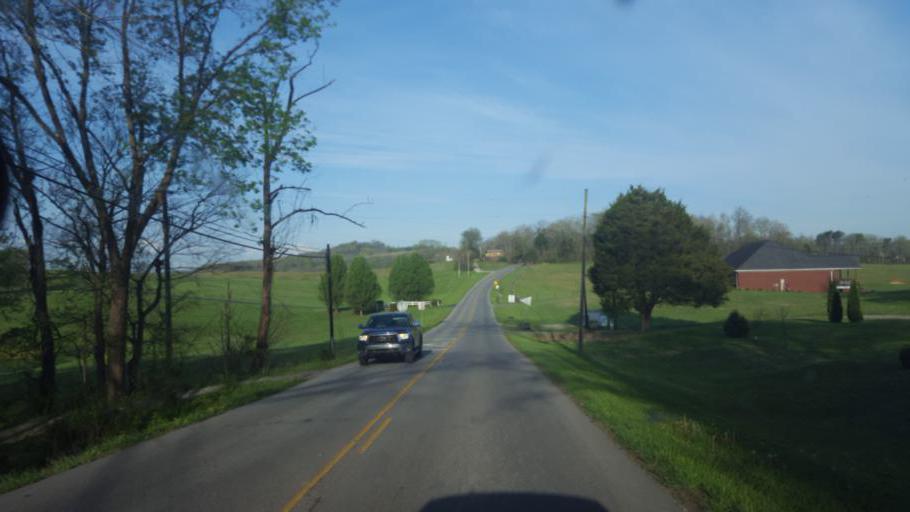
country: US
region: Kentucky
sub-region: Hart County
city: Munfordville
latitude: 37.2737
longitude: -85.9042
